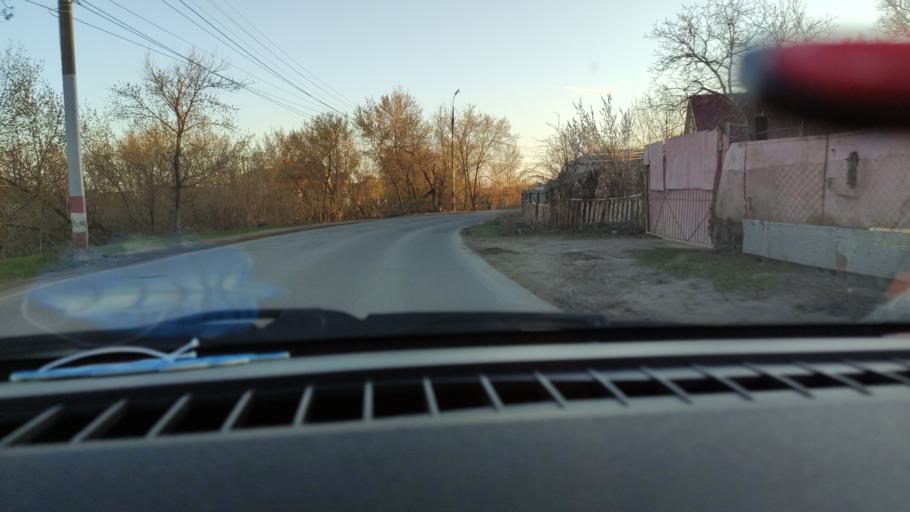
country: RU
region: Saratov
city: Engel's
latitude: 51.4966
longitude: 46.0588
